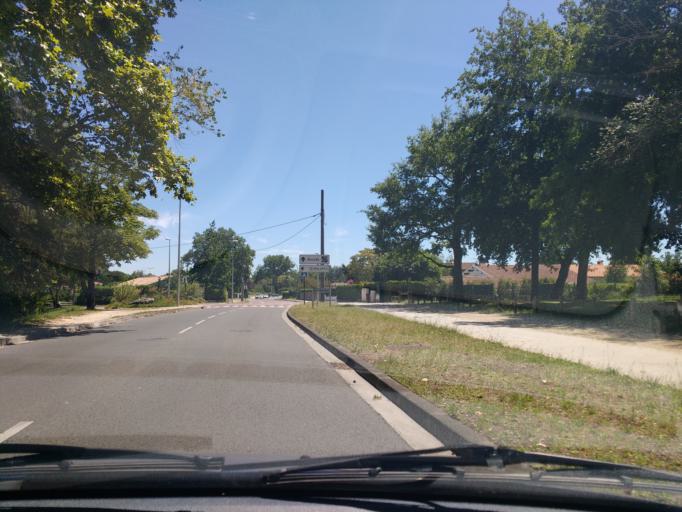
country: FR
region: Aquitaine
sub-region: Departement de la Gironde
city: Gradignan
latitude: 44.7754
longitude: -0.6036
